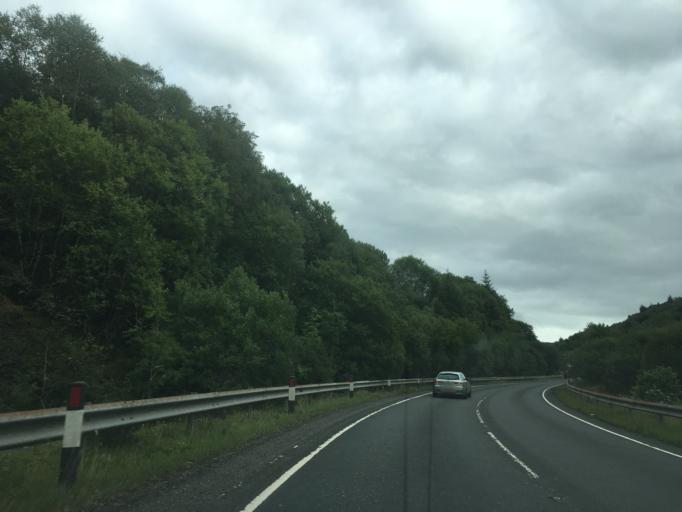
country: GB
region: Scotland
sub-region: Argyll and Bute
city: Oban
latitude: 56.3118
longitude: -5.4701
